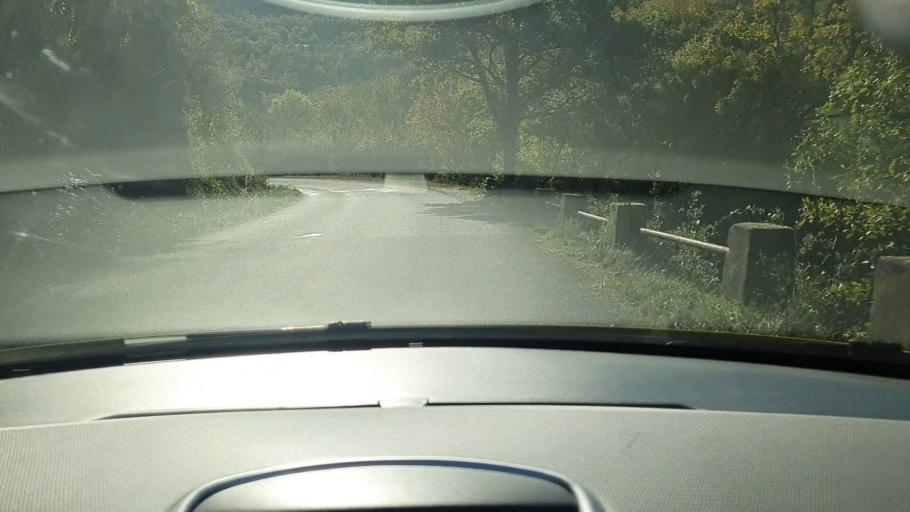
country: FR
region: Languedoc-Roussillon
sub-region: Departement du Gard
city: Le Vigan
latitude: 43.9801
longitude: 3.4962
